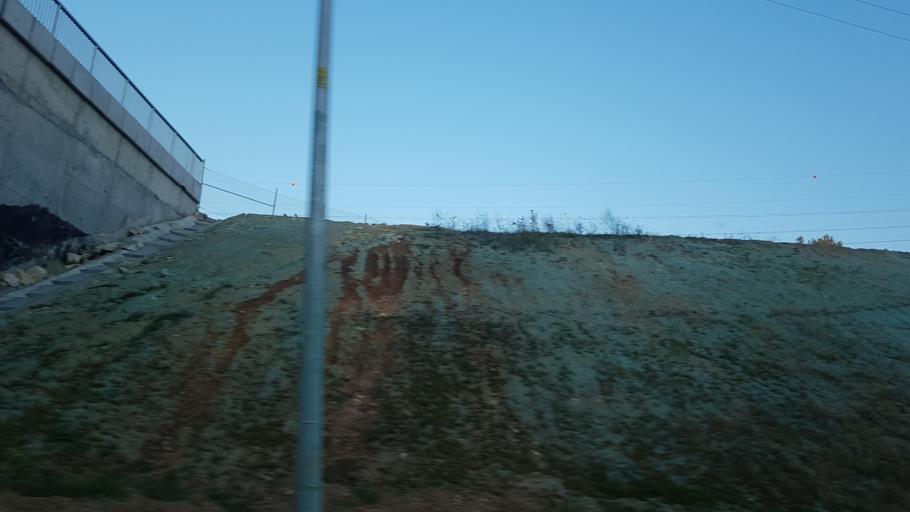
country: TR
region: Kocaeli
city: Tavsanli
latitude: 40.8036
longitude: 29.5199
